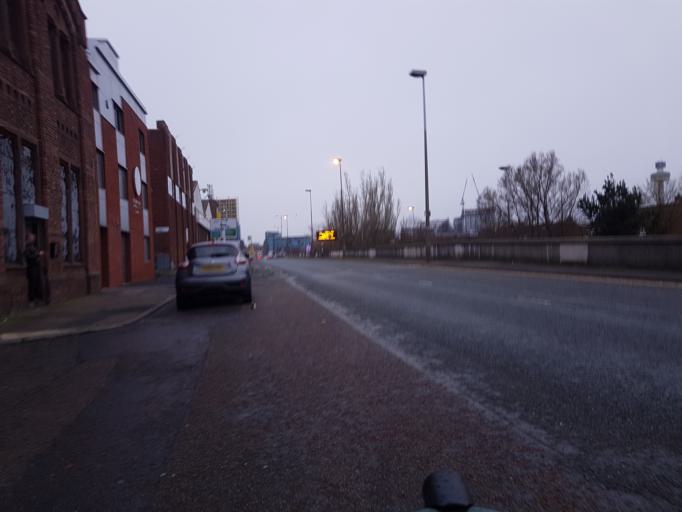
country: GB
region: England
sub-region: Liverpool
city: Liverpool
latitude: 53.4140
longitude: -2.9778
